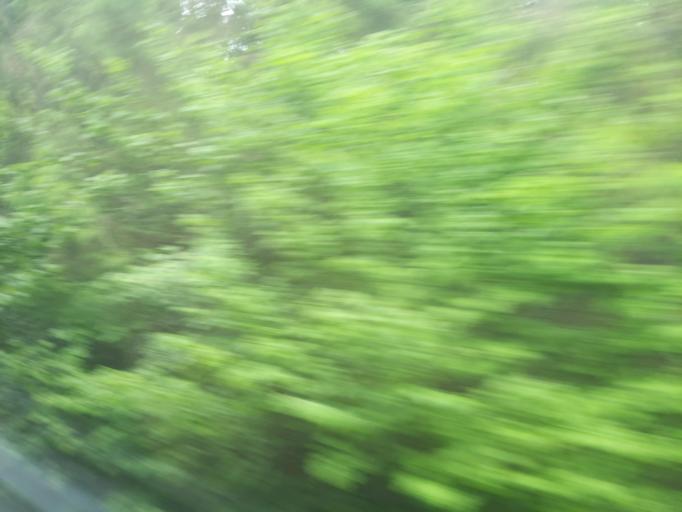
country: GB
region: England
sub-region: Devon
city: Winkleigh
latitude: 50.9236
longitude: -3.9008
